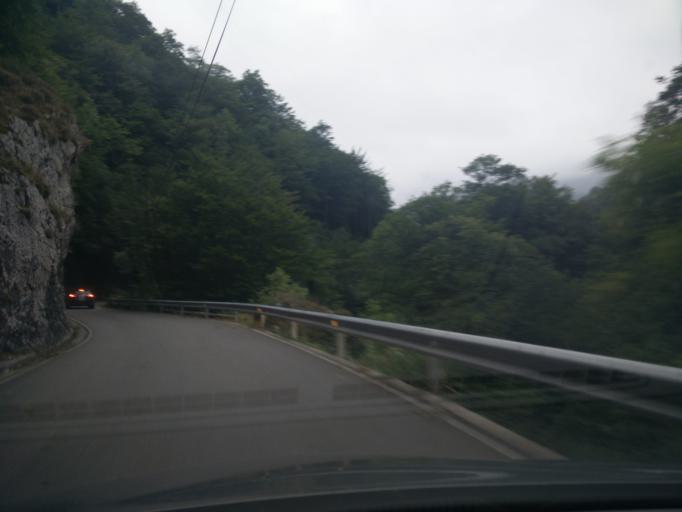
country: ES
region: Asturias
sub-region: Province of Asturias
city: Campo de Caso
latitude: 43.1638
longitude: -5.3924
